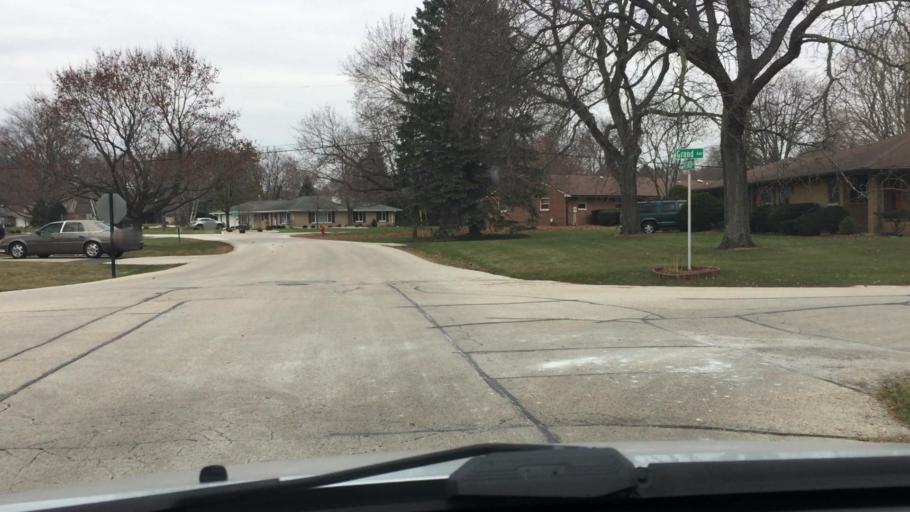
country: US
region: Wisconsin
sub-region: Ozaukee County
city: Thiensville
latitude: 43.2372
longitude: -87.9788
